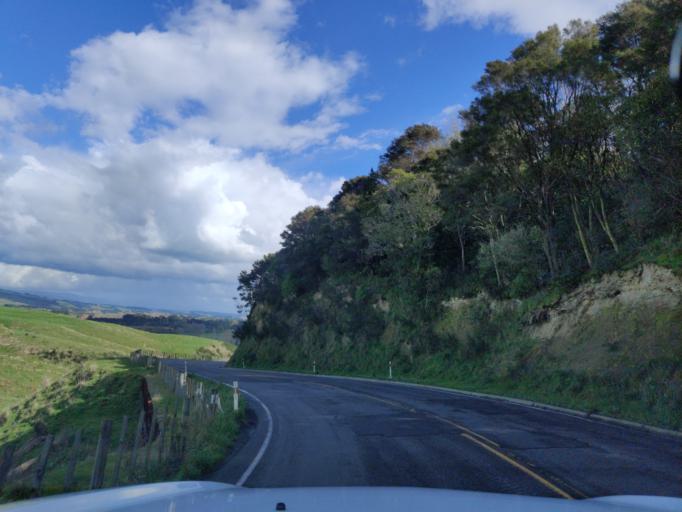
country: NZ
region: Manawatu-Wanganui
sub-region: Palmerston North City
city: Palmerston North
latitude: -40.2845
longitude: 175.7750
